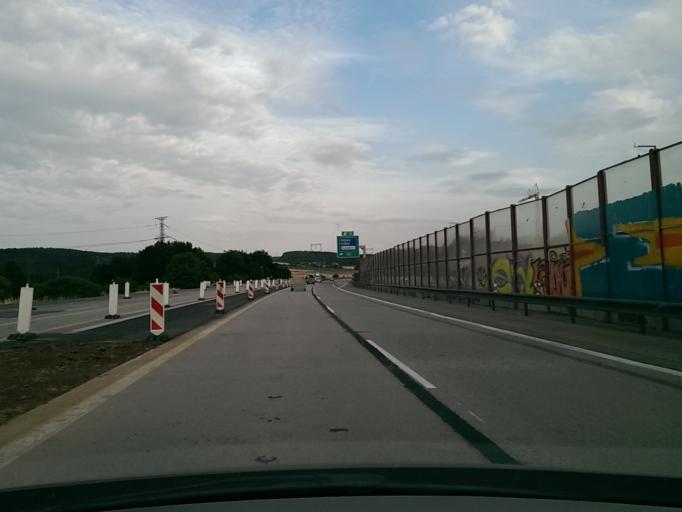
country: CZ
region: South Moravian
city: Ricany
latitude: 49.2175
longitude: 16.4081
